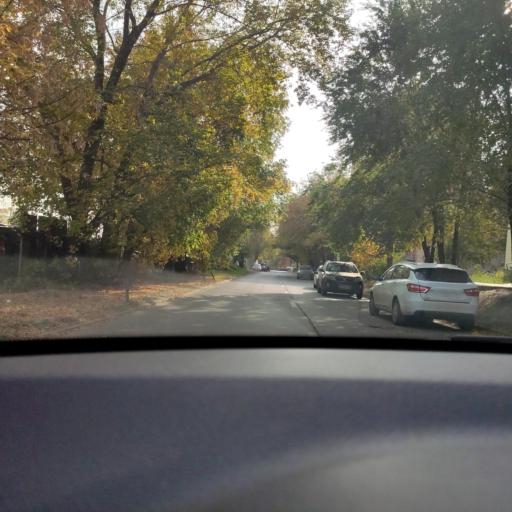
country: RU
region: Samara
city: Samara
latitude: 53.1935
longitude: 50.1997
